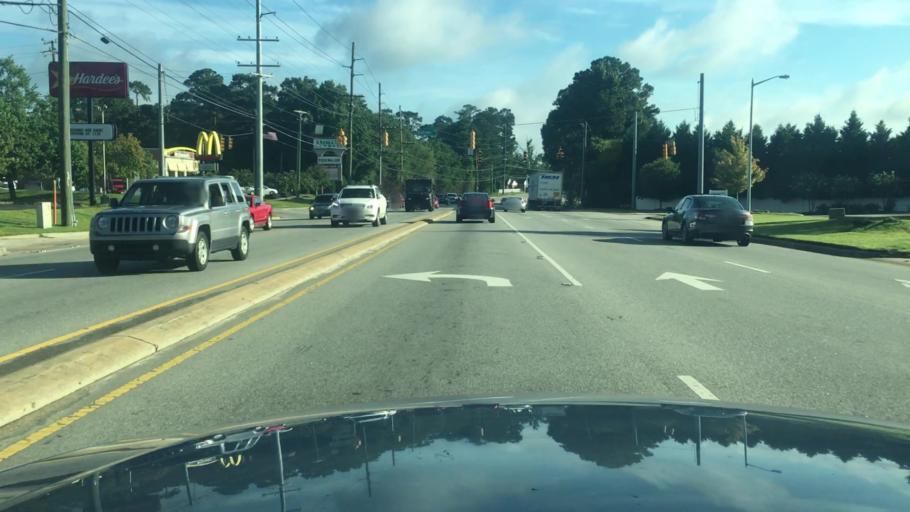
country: US
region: North Carolina
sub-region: Cumberland County
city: Eastover
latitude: 35.1568
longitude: -78.8694
